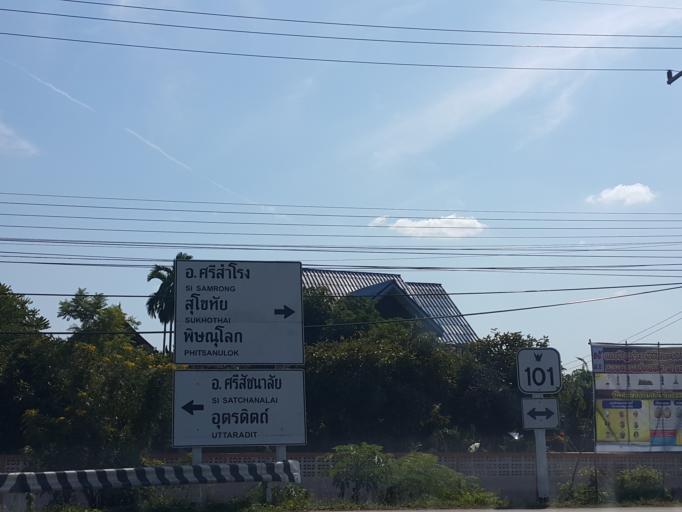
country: TH
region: Sukhothai
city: Sawankhalok
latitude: 17.2779
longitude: 99.8451
